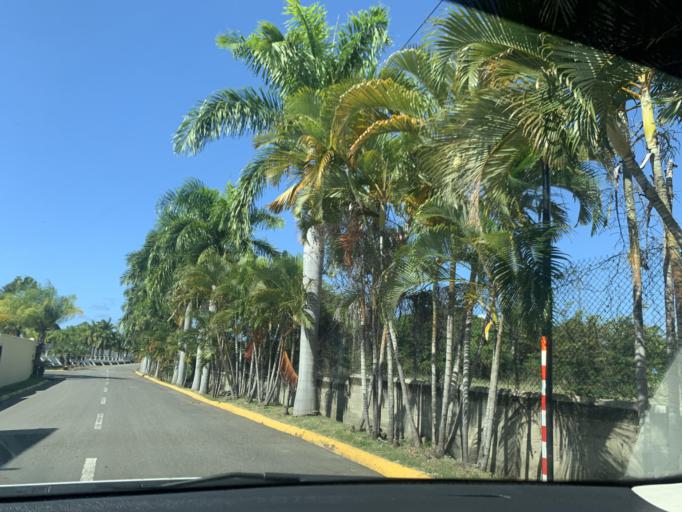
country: DO
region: Puerto Plata
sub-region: Puerto Plata
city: Puerto Plata
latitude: 19.8057
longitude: -70.7261
